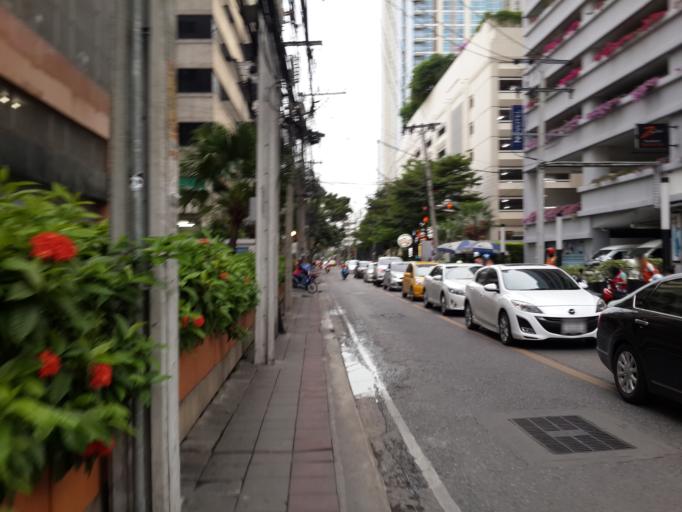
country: TH
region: Bangkok
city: Ratchathewi
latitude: 13.7426
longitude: 100.5500
